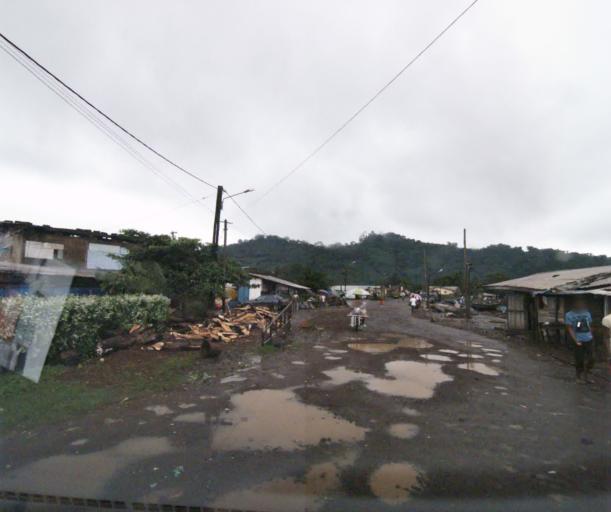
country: CM
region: South-West Province
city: Limbe
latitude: 4.0013
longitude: 9.2117
